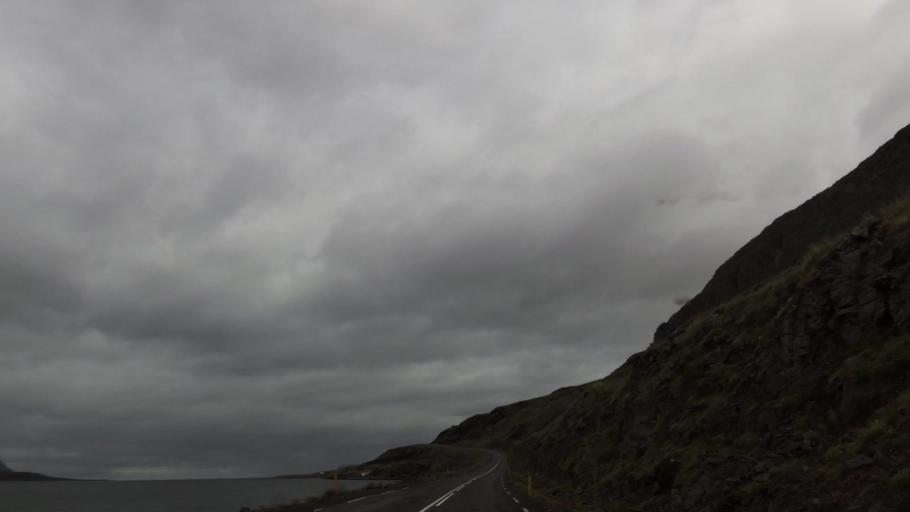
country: IS
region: Westfjords
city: Isafjoerdur
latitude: 65.9926
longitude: -22.7785
